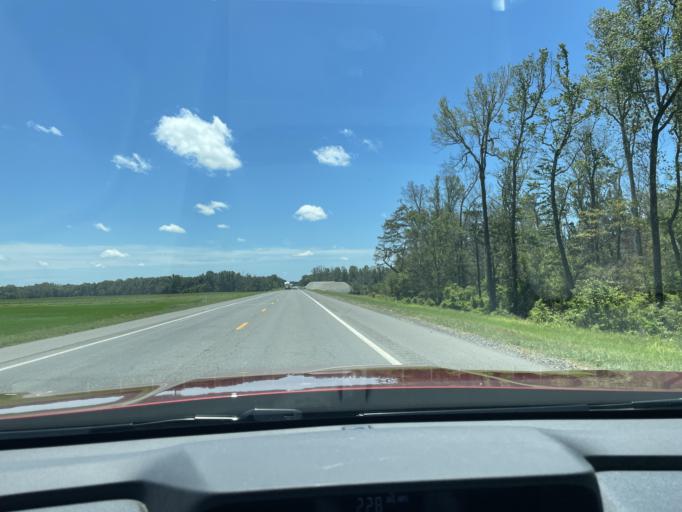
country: US
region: Arkansas
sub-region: Jefferson County
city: Pine Bluff
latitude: 34.1498
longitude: -91.9786
